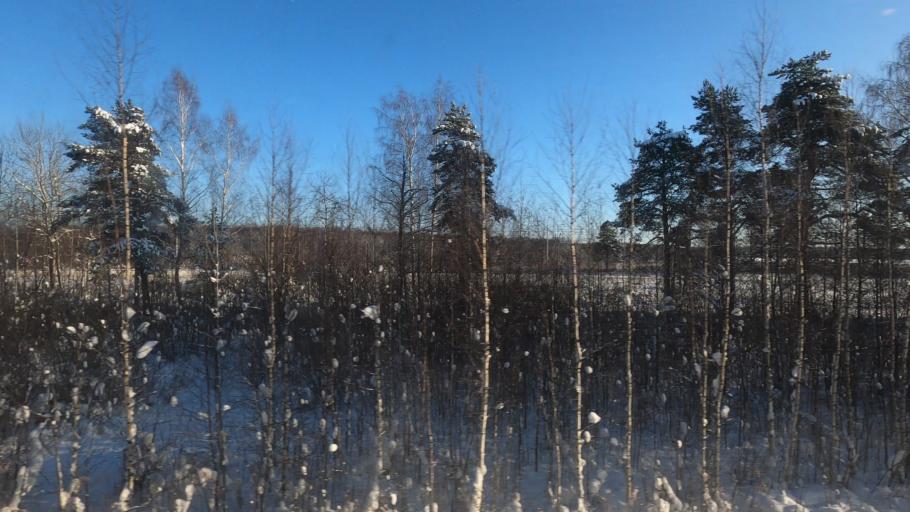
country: RU
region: Moskovskaya
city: Orud'yevo
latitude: 56.4522
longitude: 37.5259
